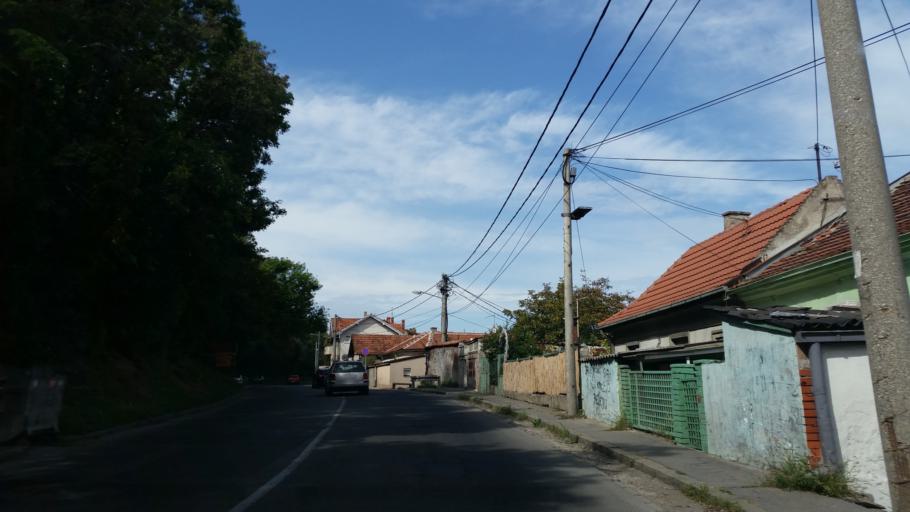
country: RS
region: Central Serbia
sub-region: Belgrade
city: Palilula
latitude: 44.8121
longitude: 20.5057
